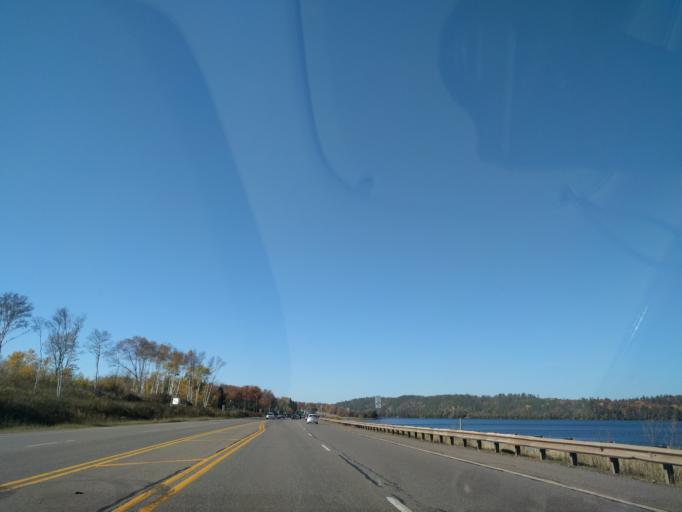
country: US
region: Michigan
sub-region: Marquette County
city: Negaunee
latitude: 46.5085
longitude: -87.6249
